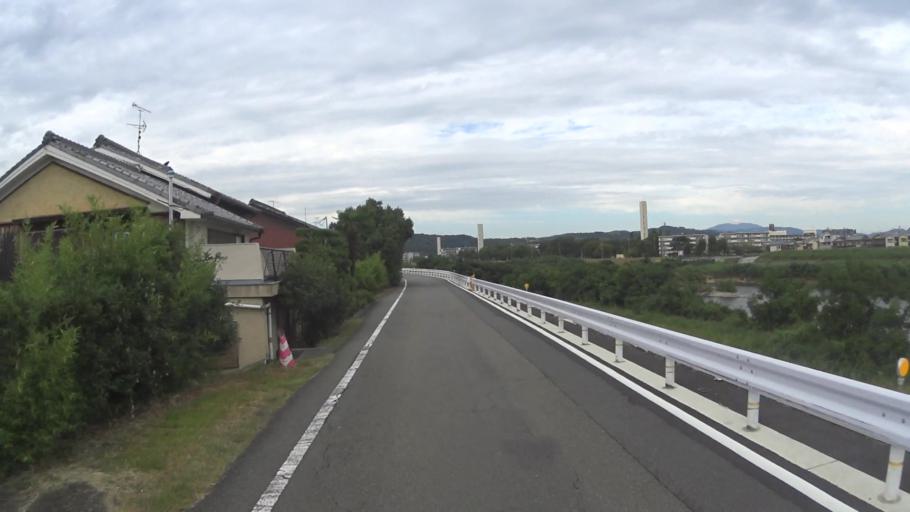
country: JP
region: Kyoto
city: Uji
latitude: 34.9190
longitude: 135.7891
